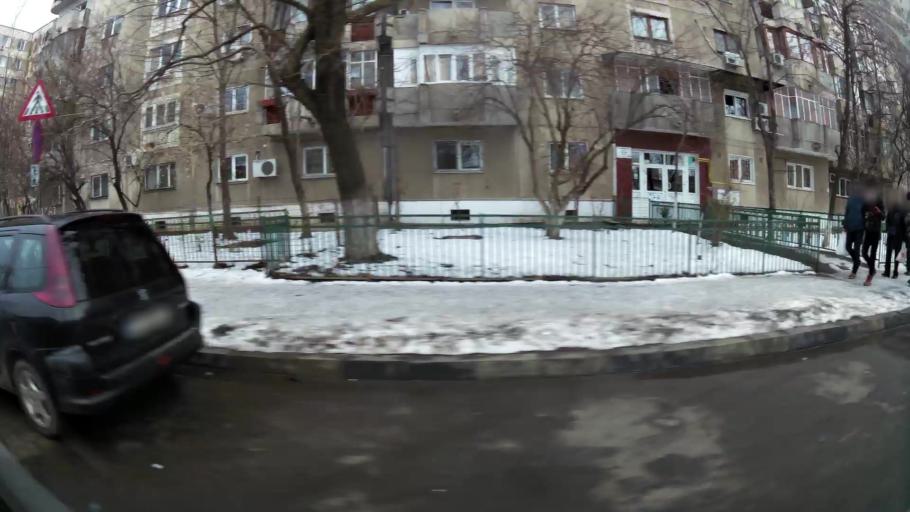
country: RO
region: Bucuresti
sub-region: Municipiul Bucuresti
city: Bucuresti
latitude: 44.4052
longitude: 26.0578
